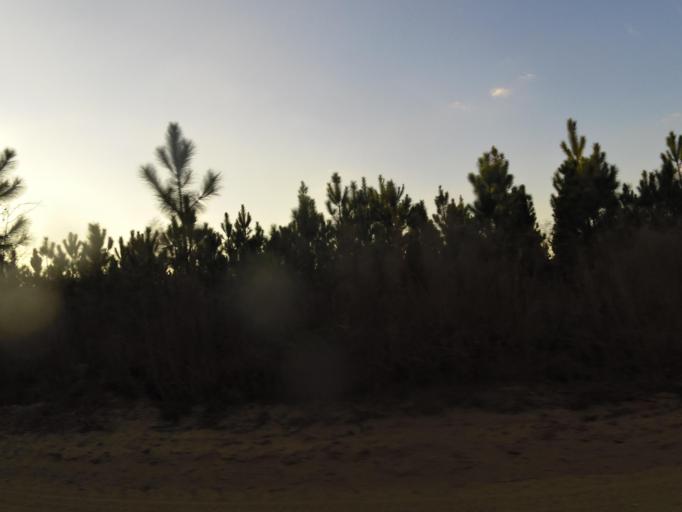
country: US
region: Florida
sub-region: Clay County
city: Keystone Heights
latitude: 29.8144
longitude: -81.8398
